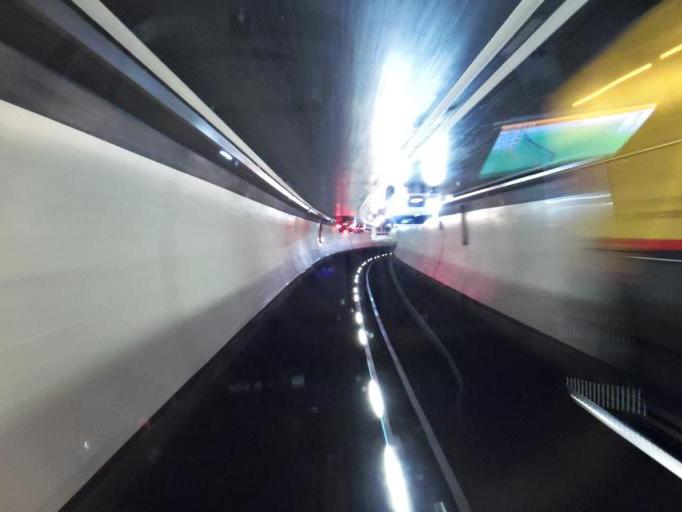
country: CH
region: Grisons
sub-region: Hinterrhein District
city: Thusis
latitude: 46.5718
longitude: 9.4145
